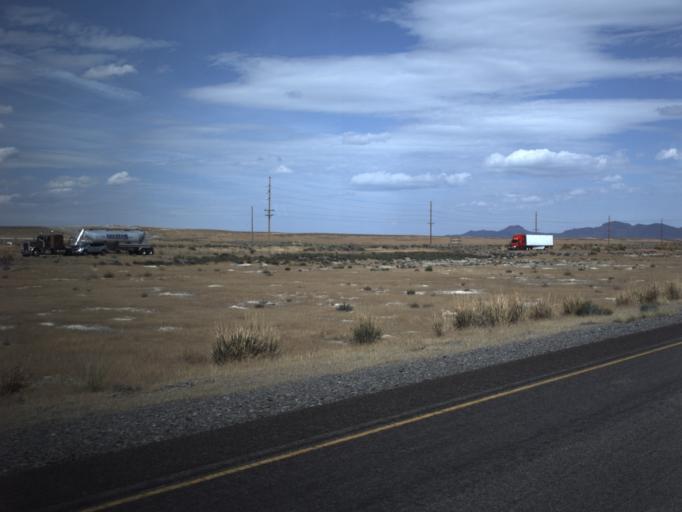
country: US
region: Utah
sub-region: Tooele County
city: Grantsville
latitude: 40.7613
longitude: -113.0051
